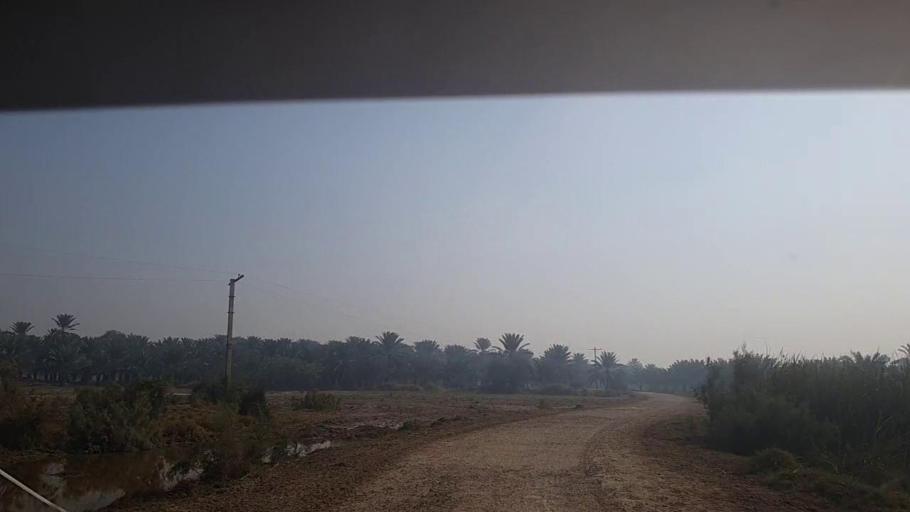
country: PK
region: Sindh
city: Khairpur
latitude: 27.4795
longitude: 68.7182
